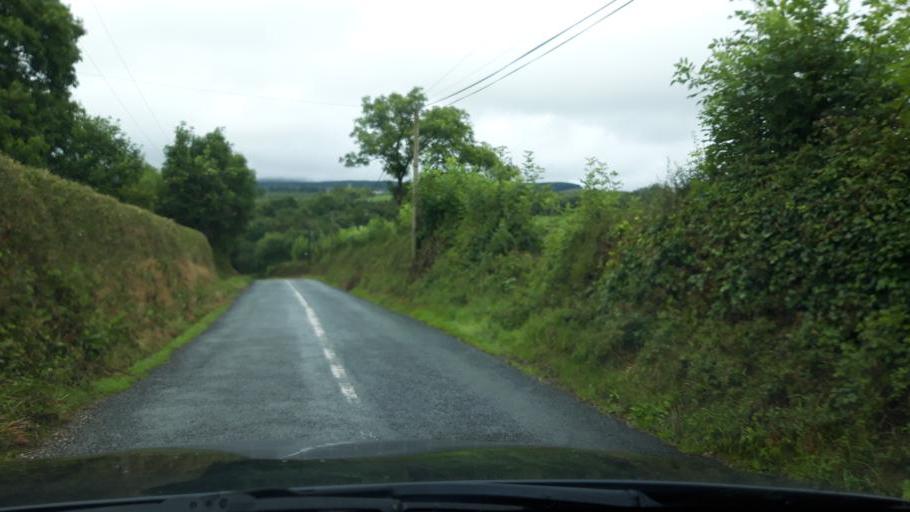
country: IE
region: Munster
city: Cahir
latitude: 52.1712
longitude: -7.8532
